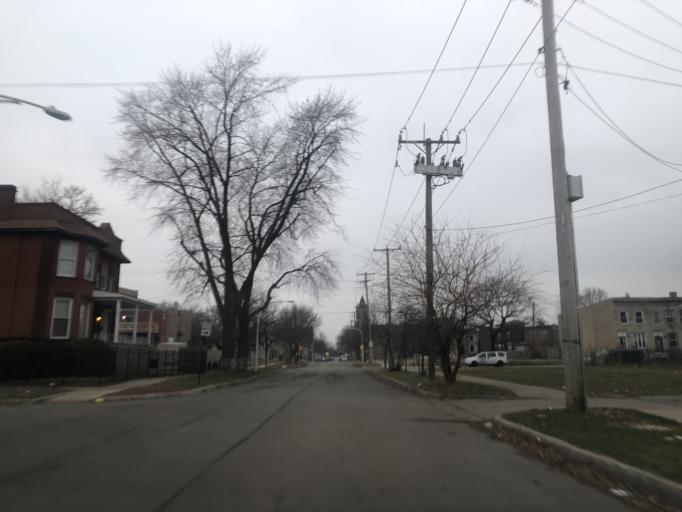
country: US
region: Illinois
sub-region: Cook County
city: Chicago
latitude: 41.7769
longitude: -87.6007
